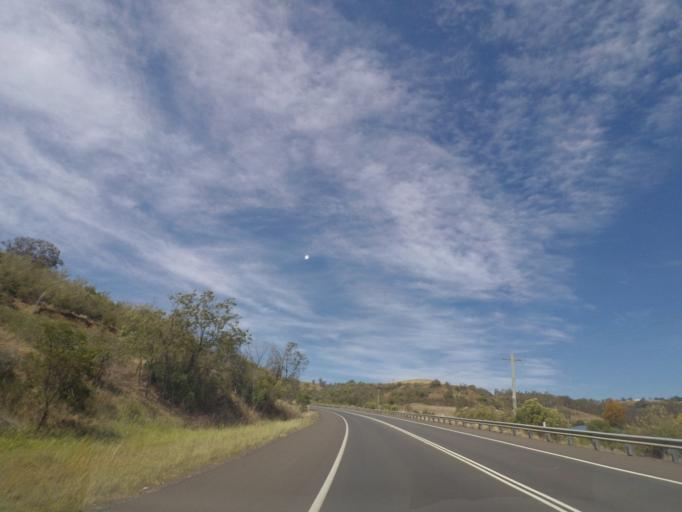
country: AU
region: New South Wales
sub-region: Wollondilly
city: Picton
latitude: -34.1608
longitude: 150.6480
